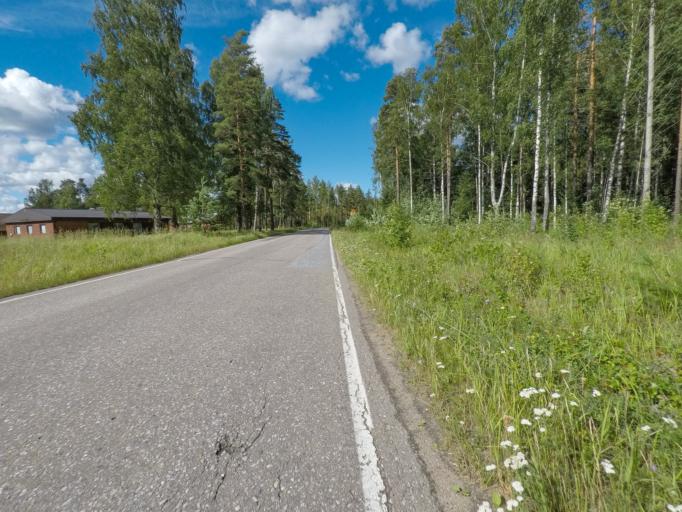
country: FI
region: South Karelia
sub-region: Lappeenranta
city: Joutseno
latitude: 61.1042
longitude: 28.3712
